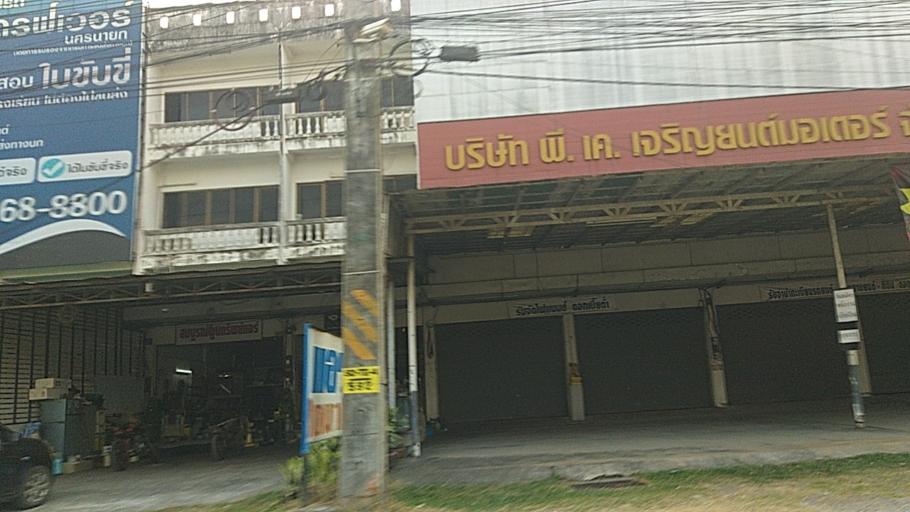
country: TH
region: Nakhon Nayok
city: Nakhon Nayok
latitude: 14.1997
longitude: 101.1925
